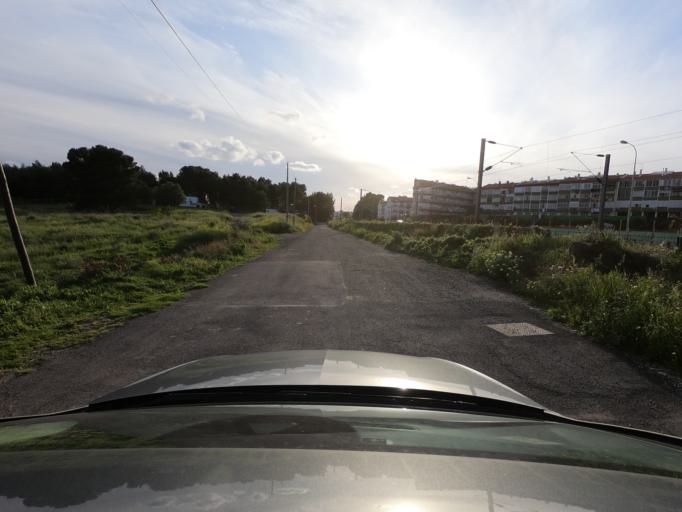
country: PT
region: Lisbon
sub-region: Oeiras
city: Oeiras
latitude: 38.6869
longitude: -9.3065
